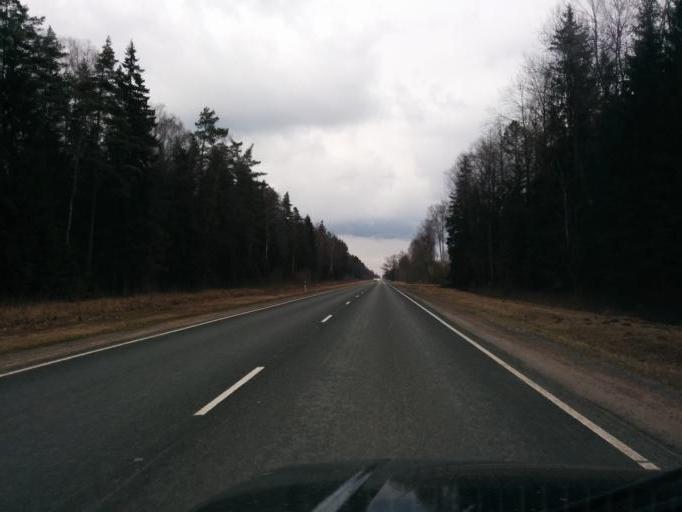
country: LV
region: Ozolnieku
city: Ozolnieki
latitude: 56.7098
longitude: 23.8264
